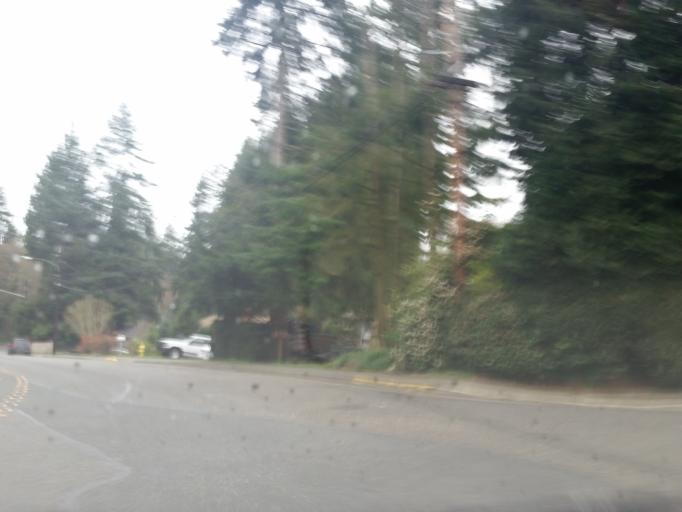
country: US
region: Washington
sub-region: Snohomish County
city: Lynnwood
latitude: 47.8261
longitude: -122.3359
